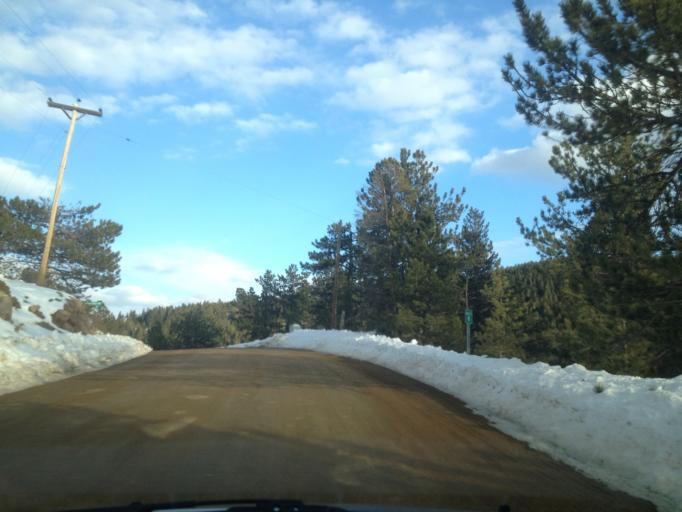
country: US
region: Colorado
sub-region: Boulder County
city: Nederland
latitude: 40.1221
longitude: -105.4503
